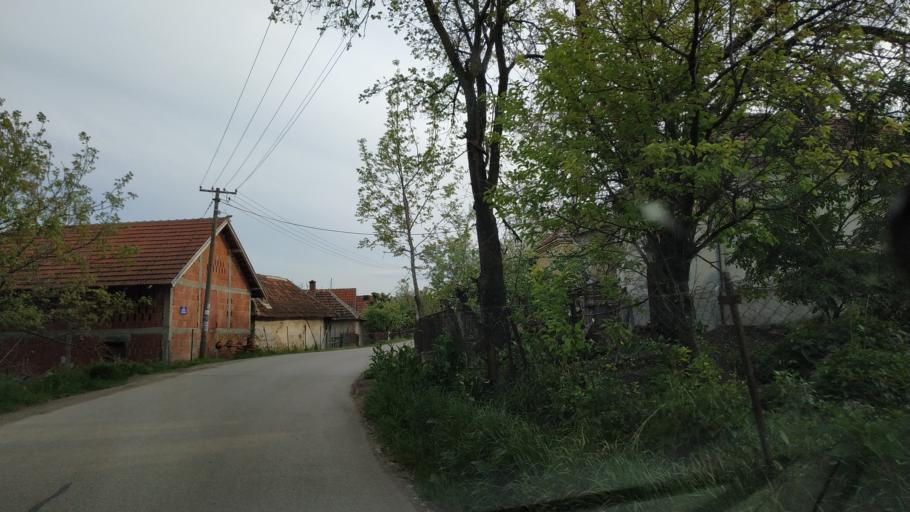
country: RS
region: Central Serbia
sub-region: Zajecarski Okrug
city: Soko Banja
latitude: 43.5267
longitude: 21.8525
